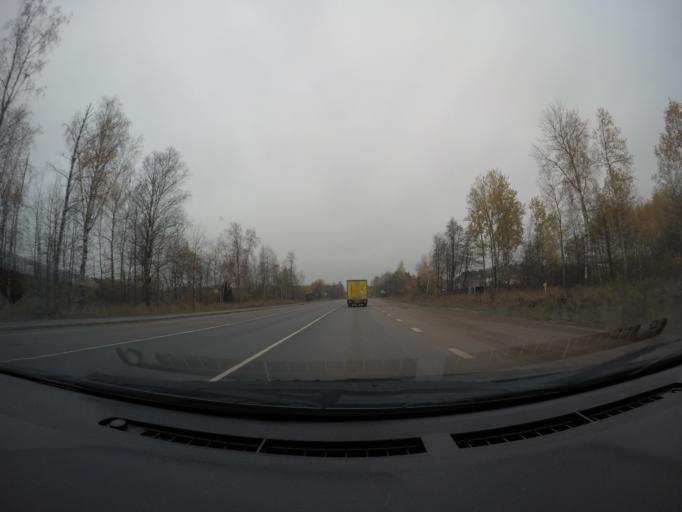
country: RU
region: Moskovskaya
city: Malyshevo
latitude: 55.5353
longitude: 38.4039
